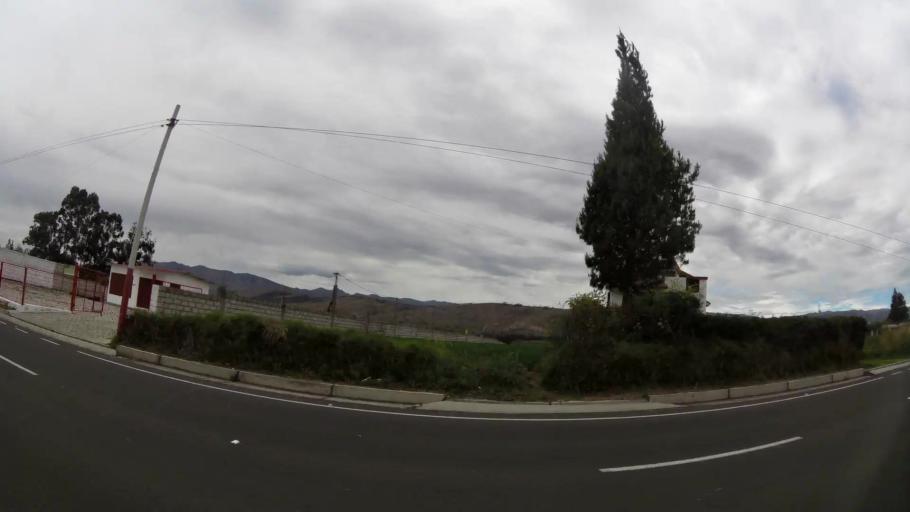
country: EC
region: Cotopaxi
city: San Miguel de Salcedo
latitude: -0.9942
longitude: -78.5959
